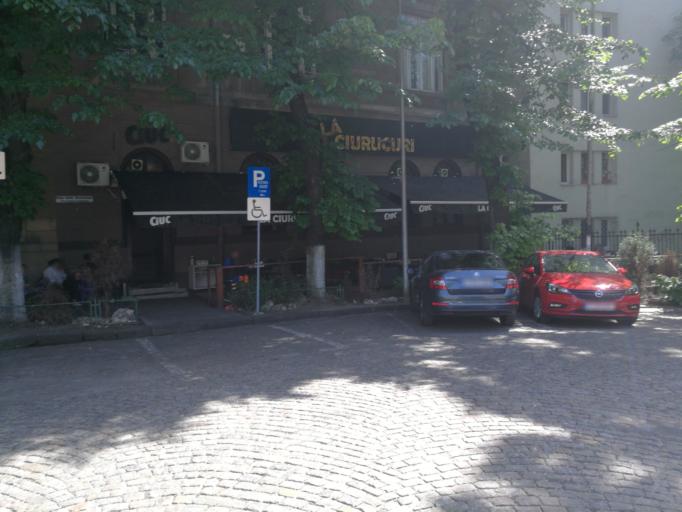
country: RO
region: Bucuresti
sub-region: Municipiul Bucuresti
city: Bucuresti
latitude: 44.4373
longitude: 26.0933
